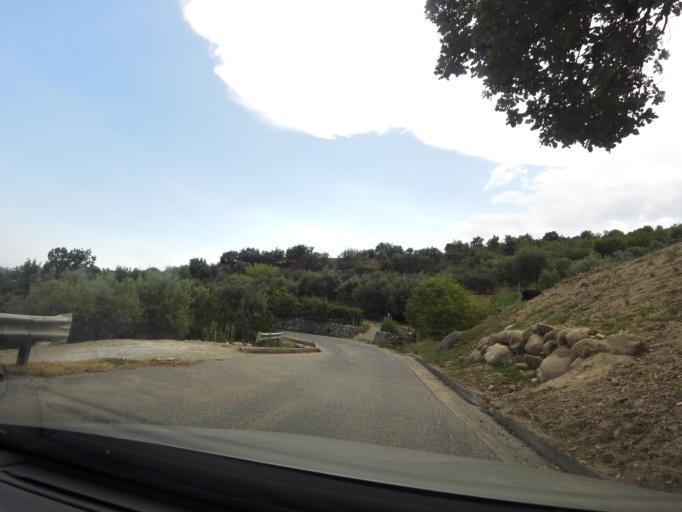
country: IT
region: Calabria
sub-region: Provincia di Reggio Calabria
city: Camini
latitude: 38.4306
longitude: 16.5137
